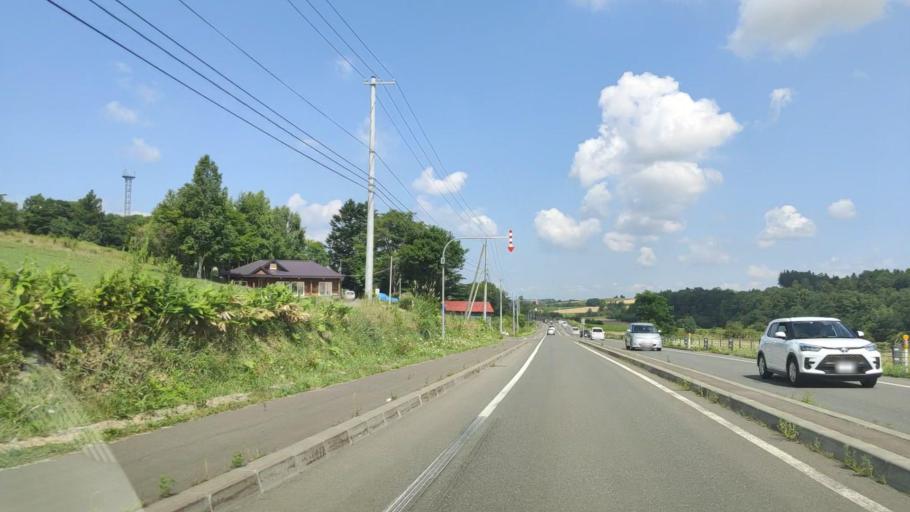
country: JP
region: Hokkaido
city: Shimo-furano
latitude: 43.5273
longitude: 142.4456
